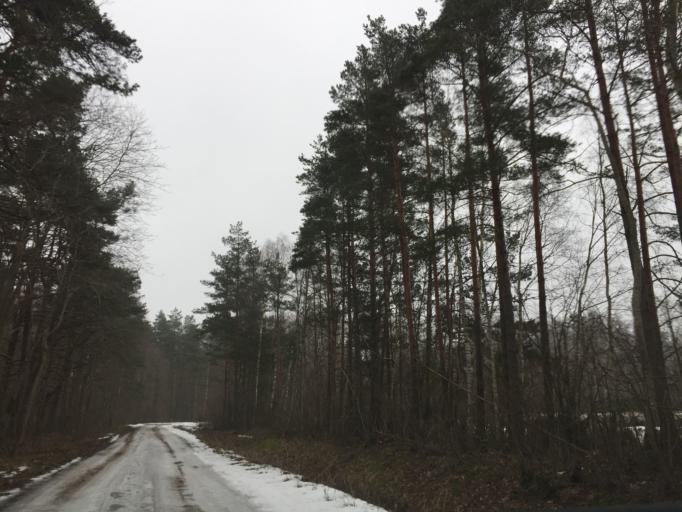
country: EE
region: Saare
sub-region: Kuressaare linn
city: Kuressaare
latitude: 58.2751
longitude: 22.5682
